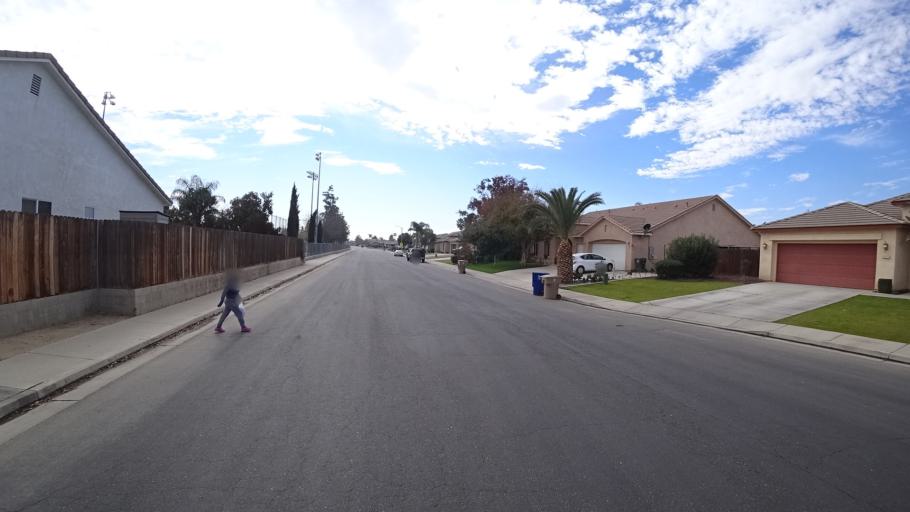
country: US
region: California
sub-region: Kern County
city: Rosedale
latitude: 35.3939
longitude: -119.1309
